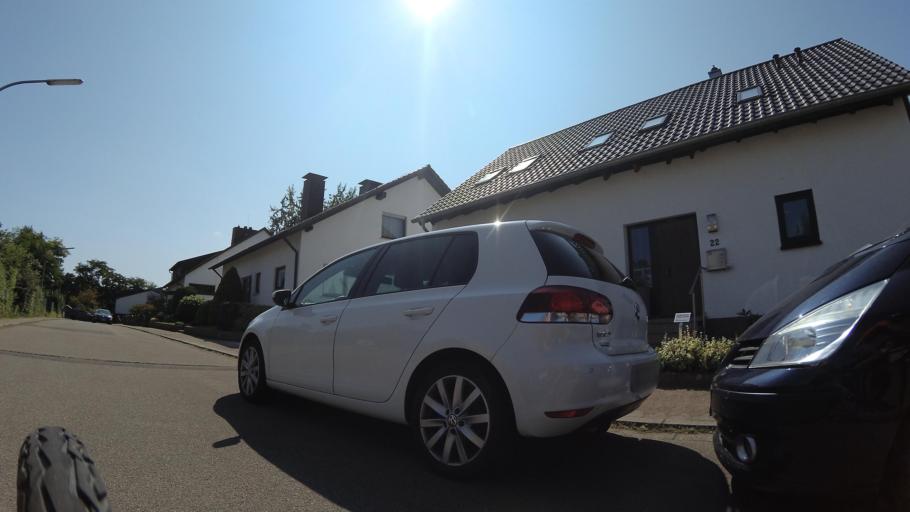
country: DE
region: Saarland
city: Saarbrucken
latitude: 49.2268
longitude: 6.9689
